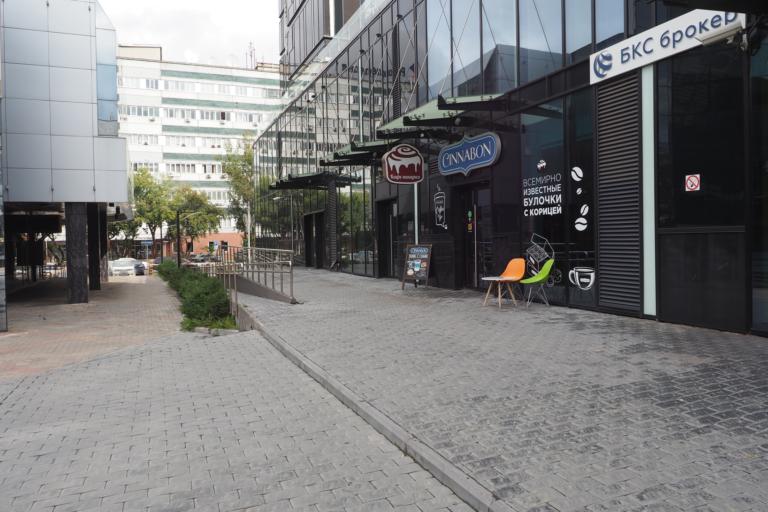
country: RU
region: Krasnoyarskiy
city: Krasnoyarsk
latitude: 56.0097
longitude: 92.8680
